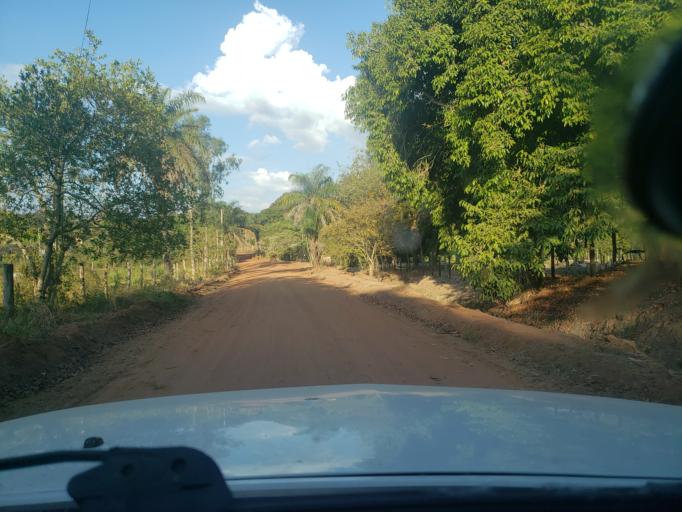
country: BR
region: Sao Paulo
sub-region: Mogi-Mirim
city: Mogi Mirim
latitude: -22.4594
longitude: -46.9389
